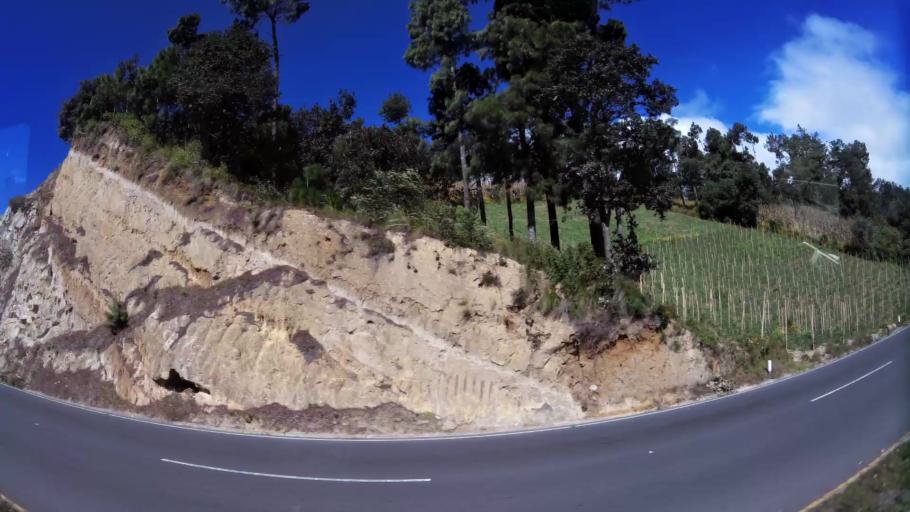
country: GT
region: Solola
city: Solola
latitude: 14.8280
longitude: -91.1837
